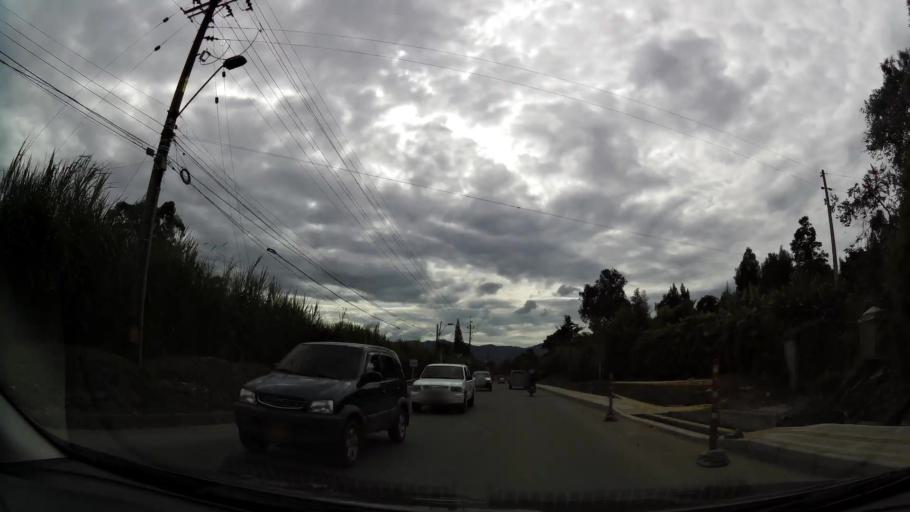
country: CO
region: Antioquia
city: Rionegro
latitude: 6.1527
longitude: -75.4035
